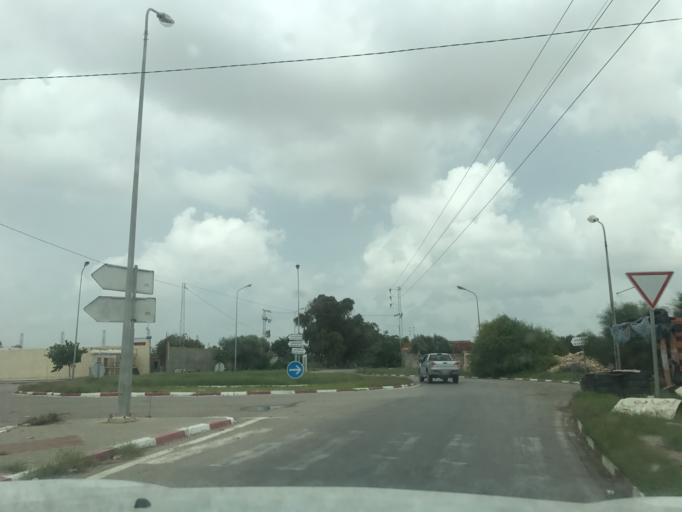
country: TN
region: Al Munastir
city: Qasr Hallal
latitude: 35.6022
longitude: 10.8992
